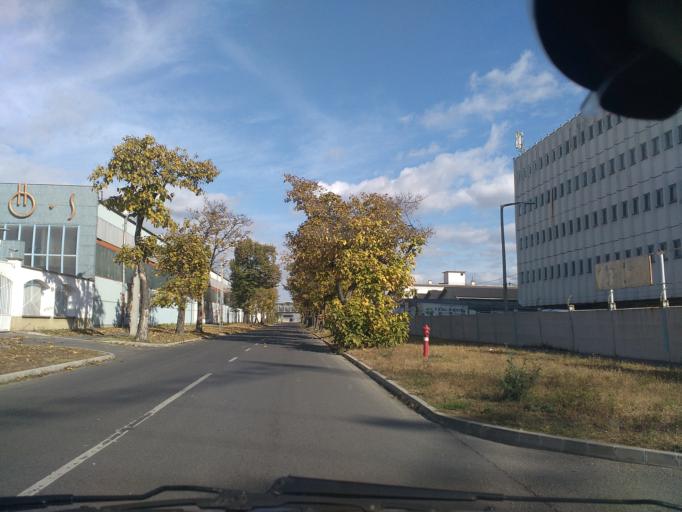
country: HU
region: Budapest
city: Budapest XIX. keruelet
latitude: 47.4713
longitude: 19.1258
